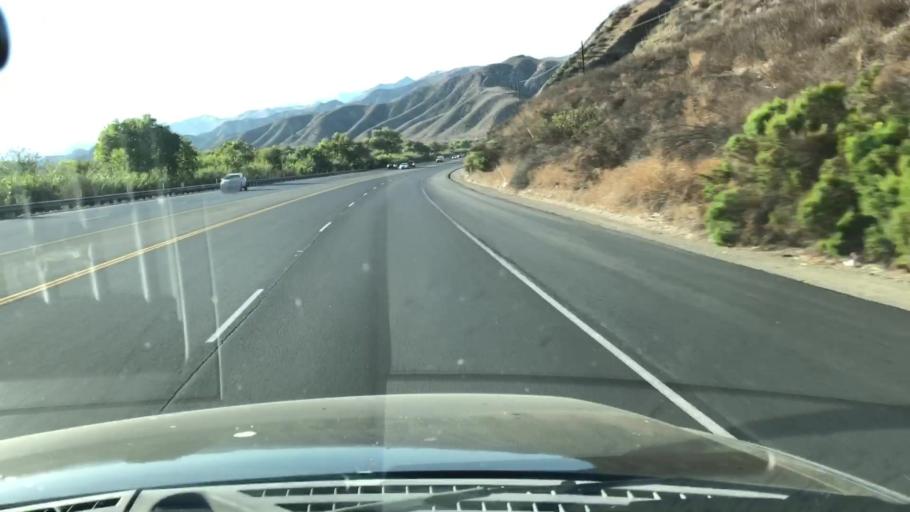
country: US
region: California
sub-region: Los Angeles County
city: Val Verde
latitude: 34.4054
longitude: -118.7192
